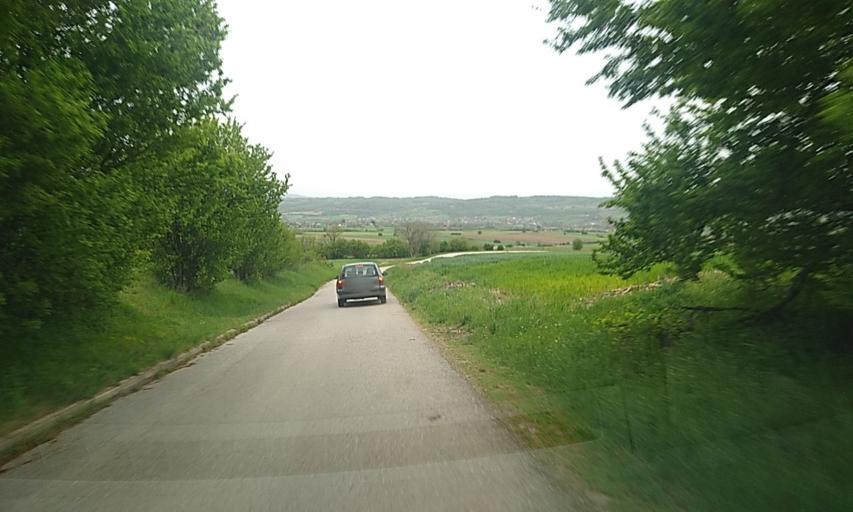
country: RS
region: Central Serbia
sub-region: Nisavski Okrug
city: Razanj
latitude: 43.5721
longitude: 21.5216
